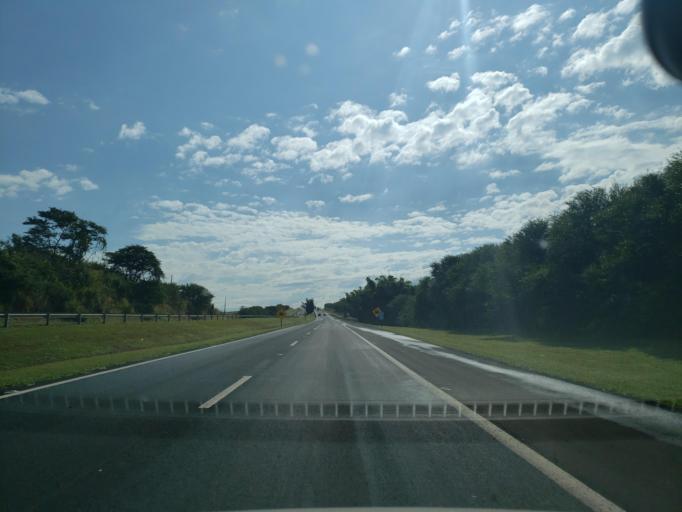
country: BR
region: Sao Paulo
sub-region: Pirajui
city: Pirajui
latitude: -22.0278
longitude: -49.4051
